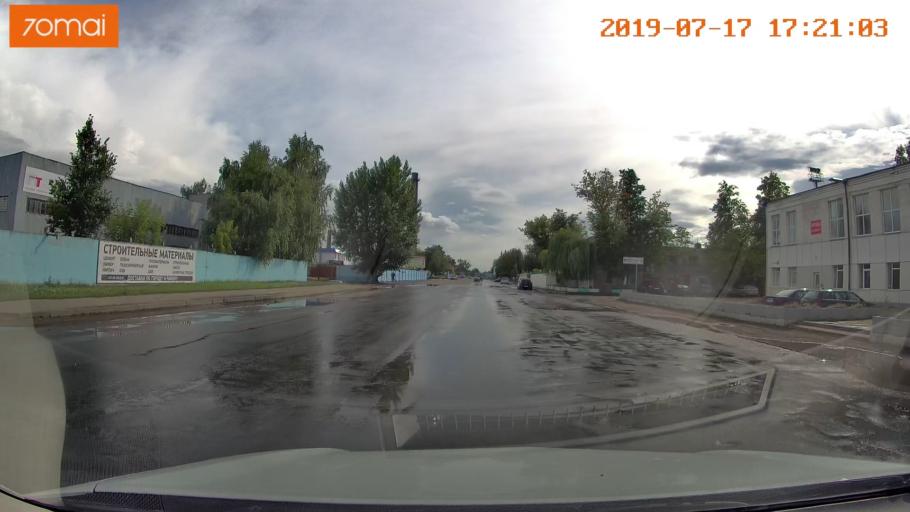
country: BY
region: Mogilev
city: Babruysk
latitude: 53.1505
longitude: 29.1819
